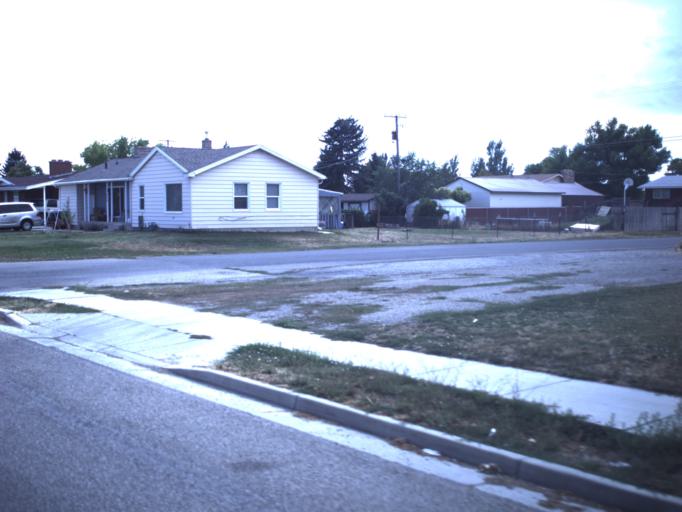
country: US
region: Utah
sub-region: Box Elder County
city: Garland
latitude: 41.7321
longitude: -112.1624
